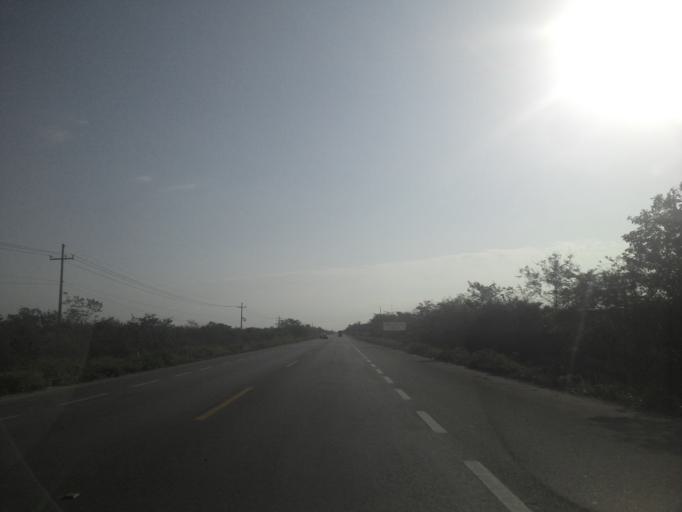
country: MX
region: Yucatan
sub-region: Valladolid
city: Tesoco
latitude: 20.6963
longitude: -88.1546
